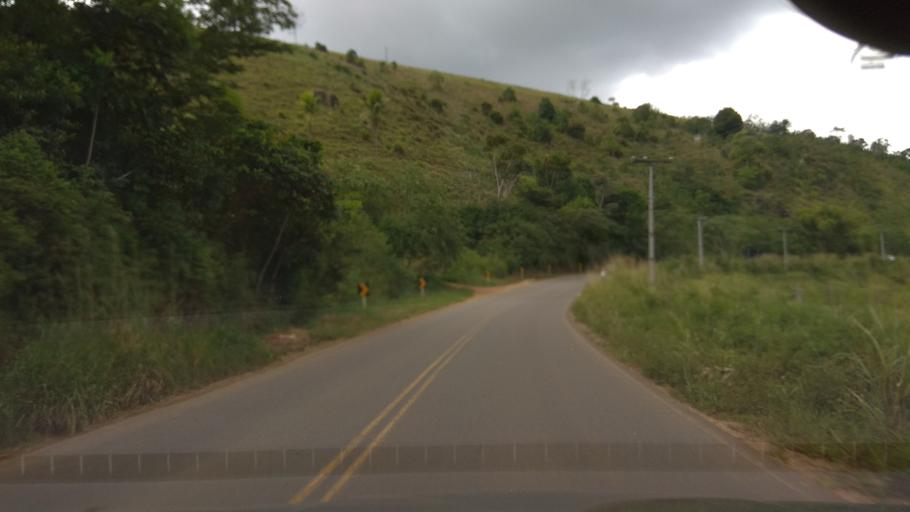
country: BR
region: Bahia
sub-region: Mutuipe
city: Mutuipe
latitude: -13.2512
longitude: -39.5638
